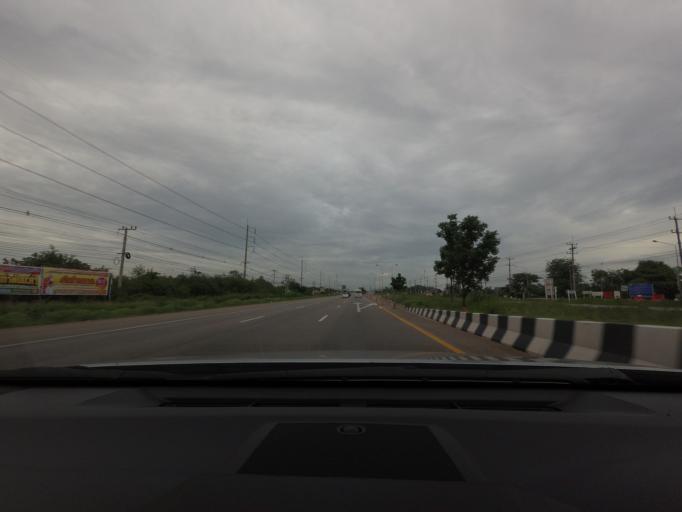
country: TH
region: Samut Songkhram
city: Amphawa
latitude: 13.3560
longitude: 99.9290
